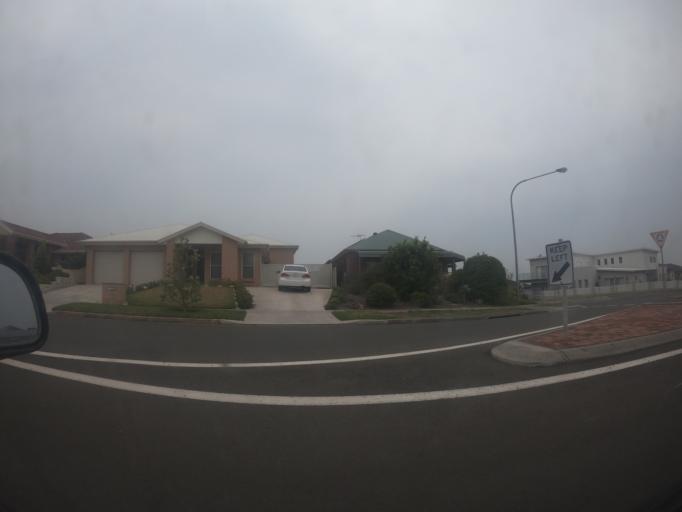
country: AU
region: New South Wales
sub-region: Shellharbour
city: Flinders
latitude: -34.5770
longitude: 150.8421
